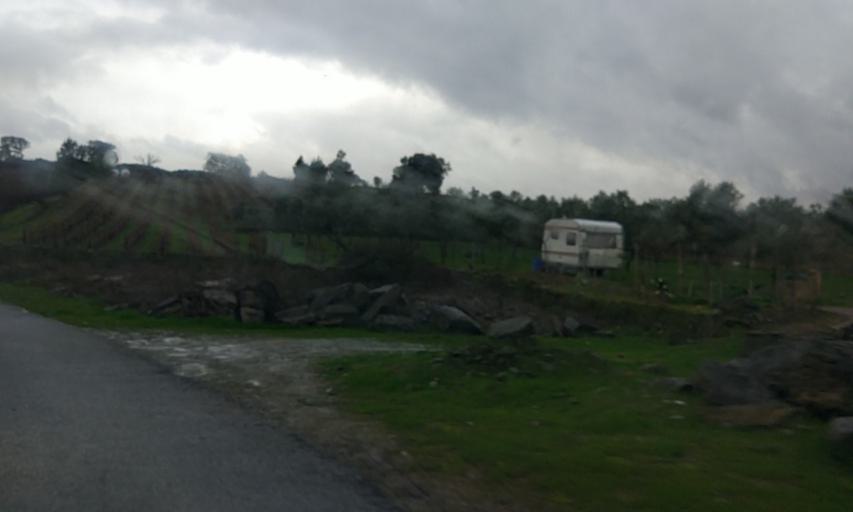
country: PT
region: Viseu
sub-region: Armamar
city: Armamar
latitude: 41.1624
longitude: -7.7110
